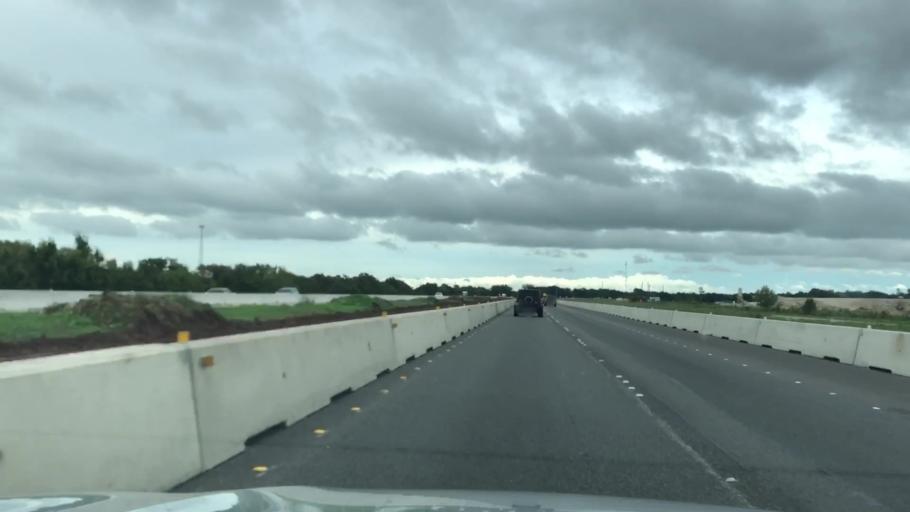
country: US
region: Texas
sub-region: Waller County
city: Brookshire
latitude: 29.7807
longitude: -96.0001
